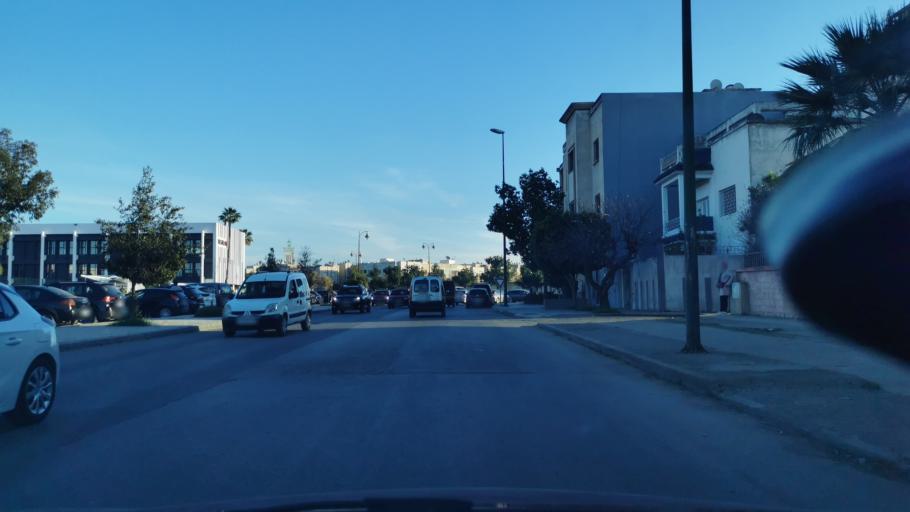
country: MA
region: Fes-Boulemane
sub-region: Fes
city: Fes
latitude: 34.0218
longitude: -4.9828
